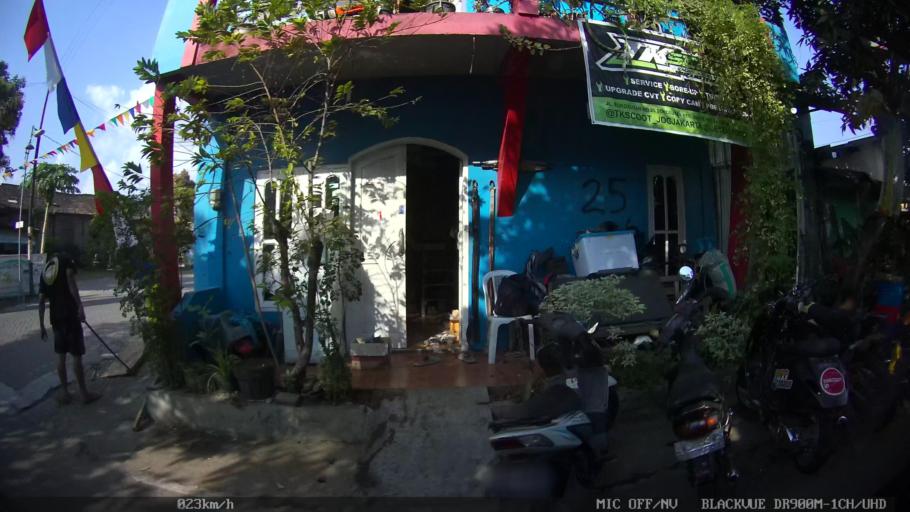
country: ID
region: Daerah Istimewa Yogyakarta
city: Yogyakarta
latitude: -7.8198
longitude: 110.3786
